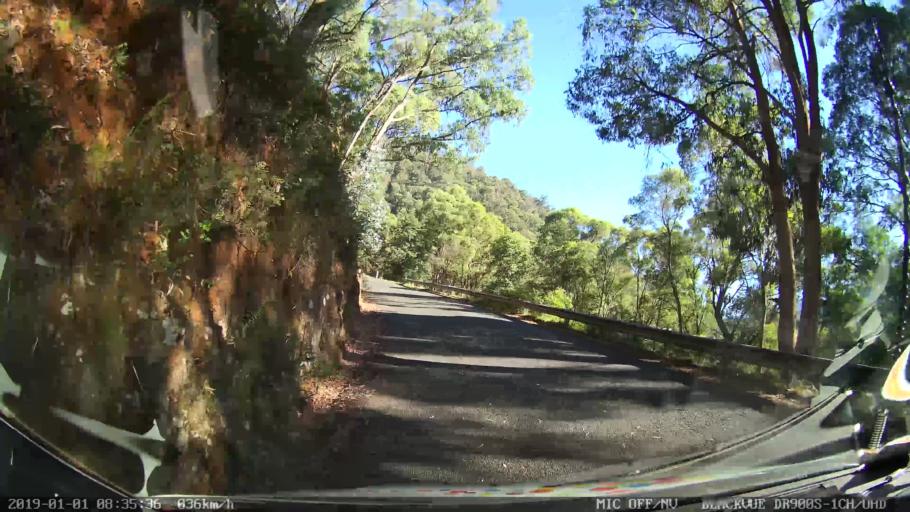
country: AU
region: New South Wales
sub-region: Snowy River
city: Jindabyne
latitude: -36.3483
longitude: 148.1939
